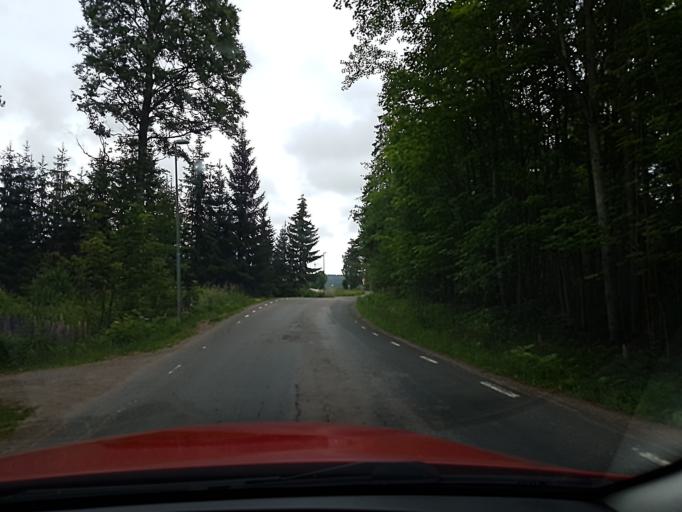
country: SE
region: Vaestra Goetaland
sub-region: Tidaholms Kommun
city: Olofstorp
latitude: 58.3048
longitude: 14.1080
